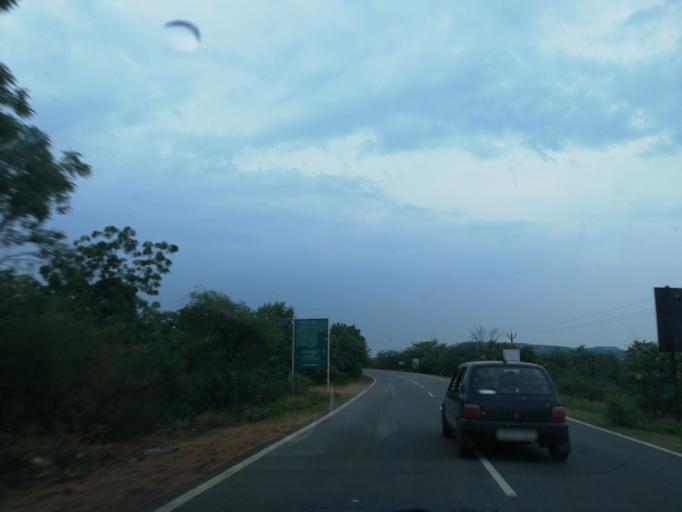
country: IN
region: Andhra Pradesh
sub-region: Guntur
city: Macherla
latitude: 16.6294
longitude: 79.2912
